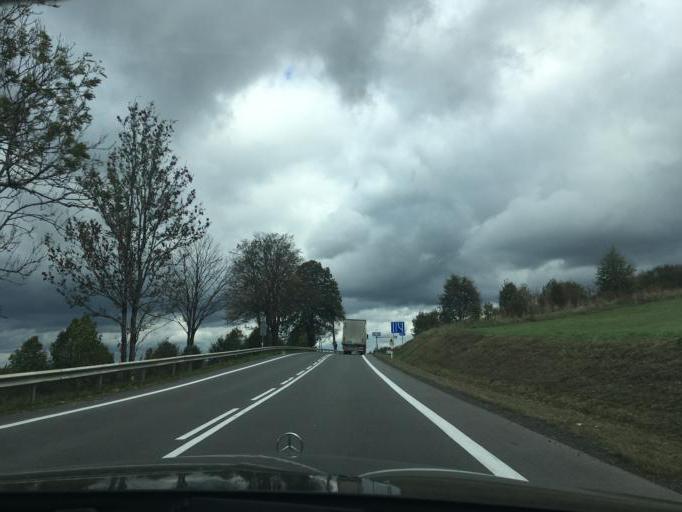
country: PL
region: Subcarpathian Voivodeship
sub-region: Powiat krosnienski
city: Dukla
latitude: 49.6024
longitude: 21.7251
